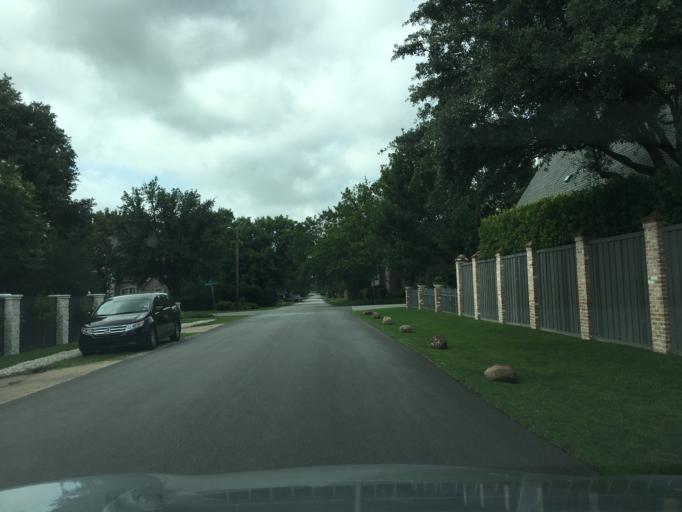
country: US
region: Texas
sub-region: Dallas County
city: University Park
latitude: 32.8857
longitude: -96.7900
